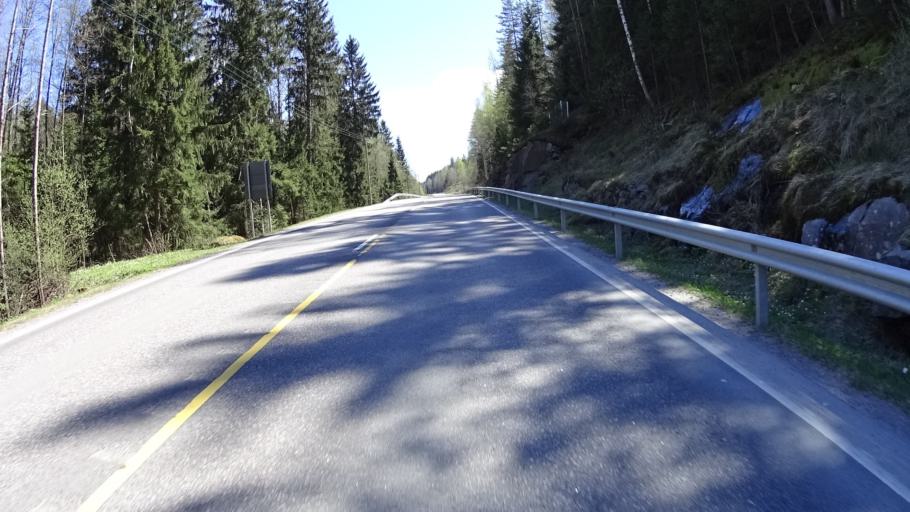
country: FI
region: Uusimaa
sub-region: Helsinki
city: Espoo
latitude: 60.3513
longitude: 24.5440
